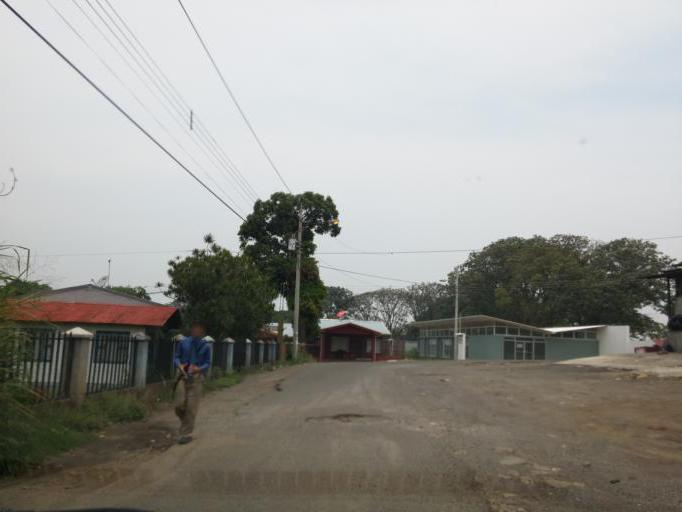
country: CR
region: Alajuela
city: Alajuela
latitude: 9.9927
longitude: -84.2061
